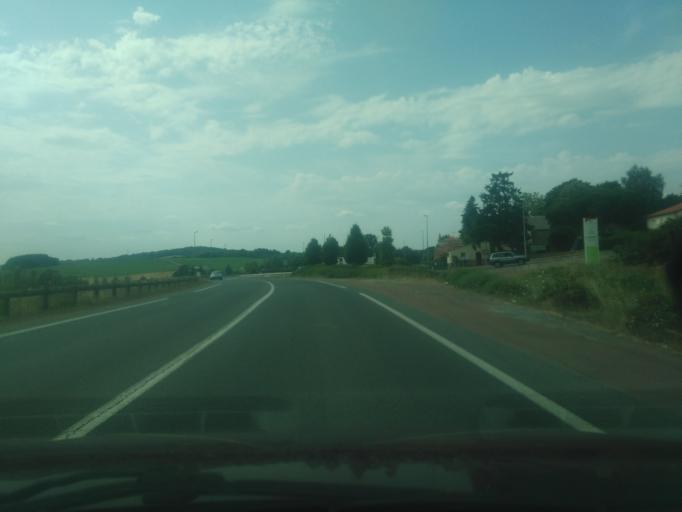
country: FR
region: Pays de la Loire
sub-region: Departement de la Vendee
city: Antigny
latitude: 46.6608
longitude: -0.7873
